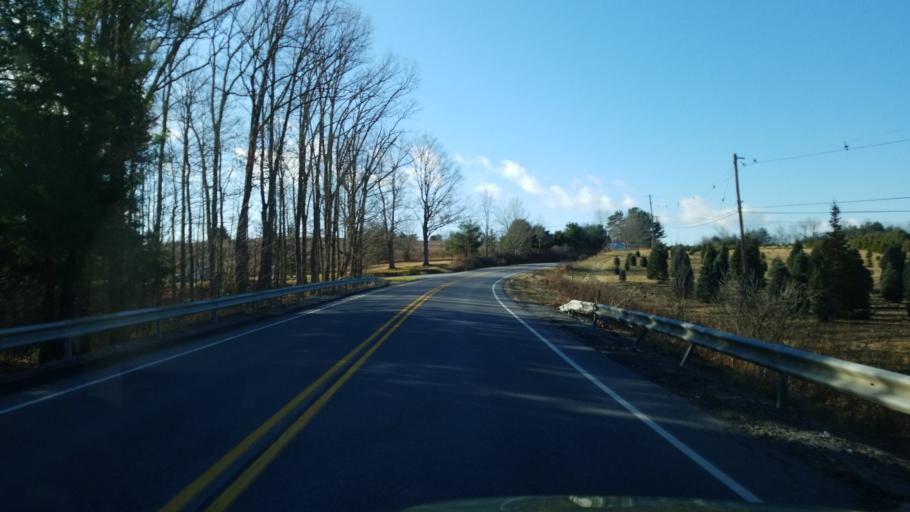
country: US
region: Pennsylvania
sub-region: Clearfield County
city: Hyde
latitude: 40.9789
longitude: -78.4529
